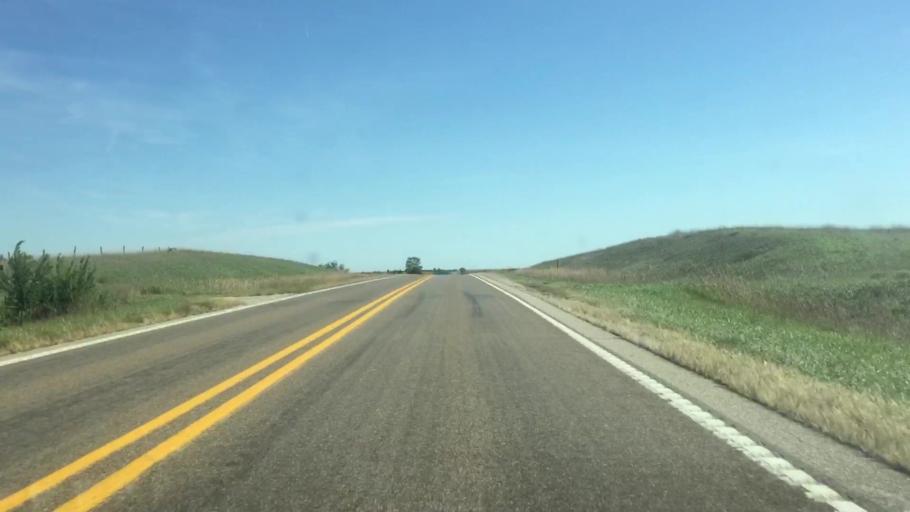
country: US
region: Nebraska
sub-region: Thayer County
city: Hebron
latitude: 40.1472
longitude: -97.5368
